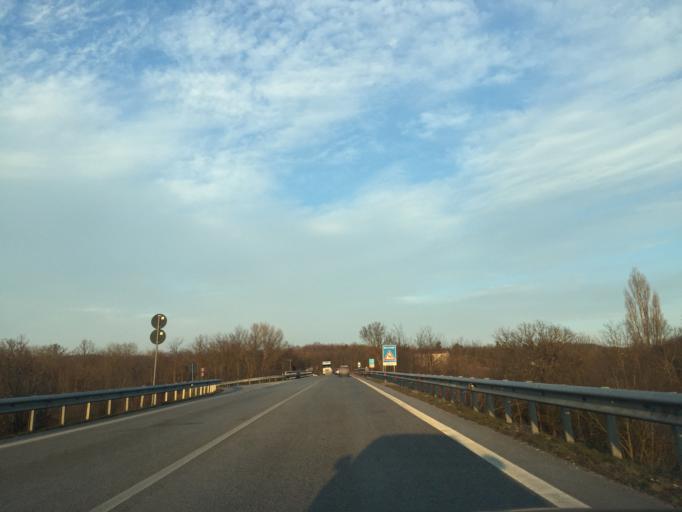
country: IT
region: Molise
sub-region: Provincia di Campobasso
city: Vinchiaturo
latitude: 41.4809
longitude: 14.5849
